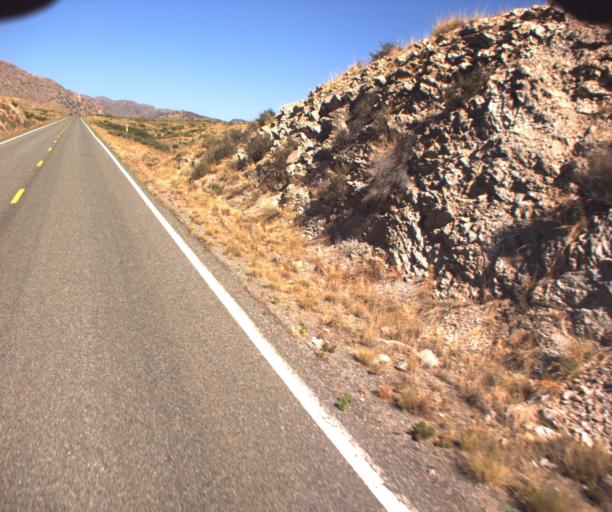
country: US
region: Arizona
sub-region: Graham County
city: Swift Trail Junction
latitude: 32.5603
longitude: -109.7634
